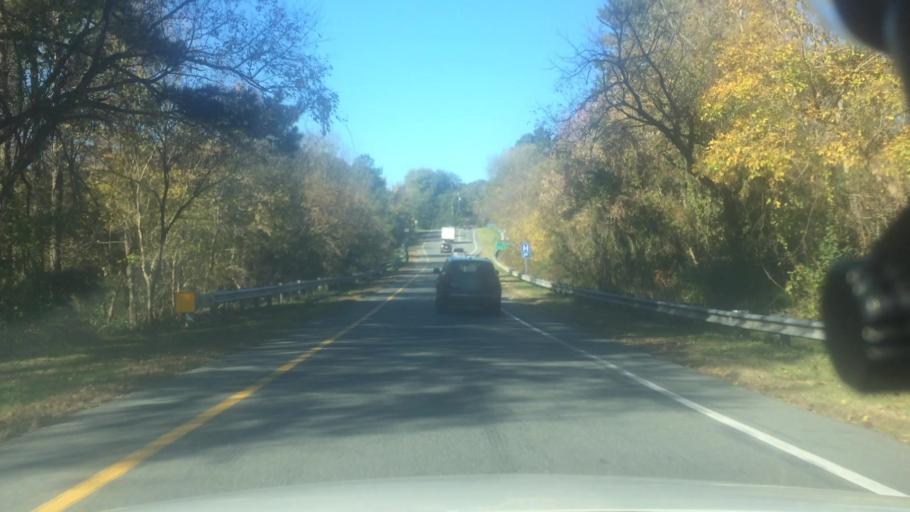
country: US
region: North Carolina
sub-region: Orange County
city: Chapel Hill
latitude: 35.8943
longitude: -79.0549
